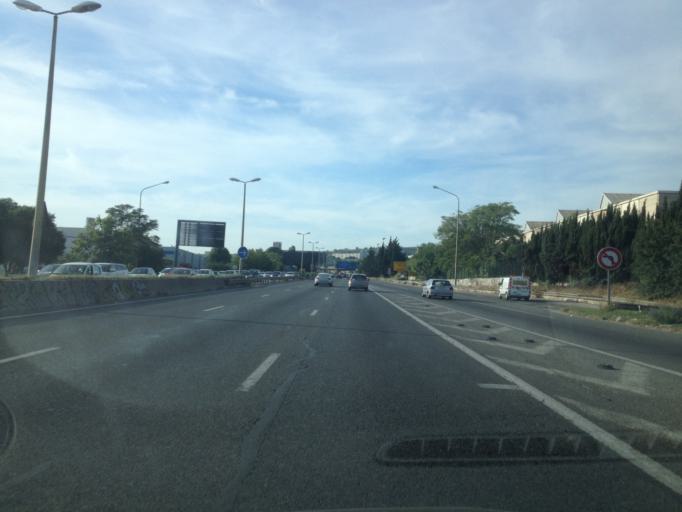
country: FR
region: Provence-Alpes-Cote d'Azur
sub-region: Departement des Bouches-du-Rhone
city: Marseille 14
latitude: 43.3336
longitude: 5.3775
